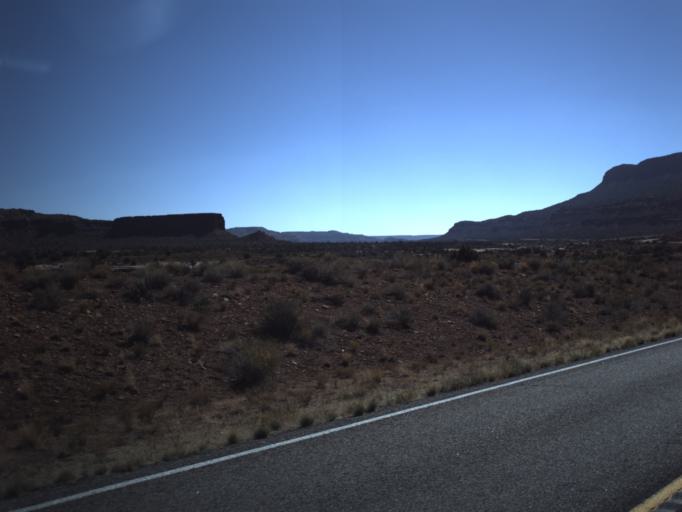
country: US
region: Utah
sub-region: San Juan County
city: Blanding
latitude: 37.6977
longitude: -110.2312
